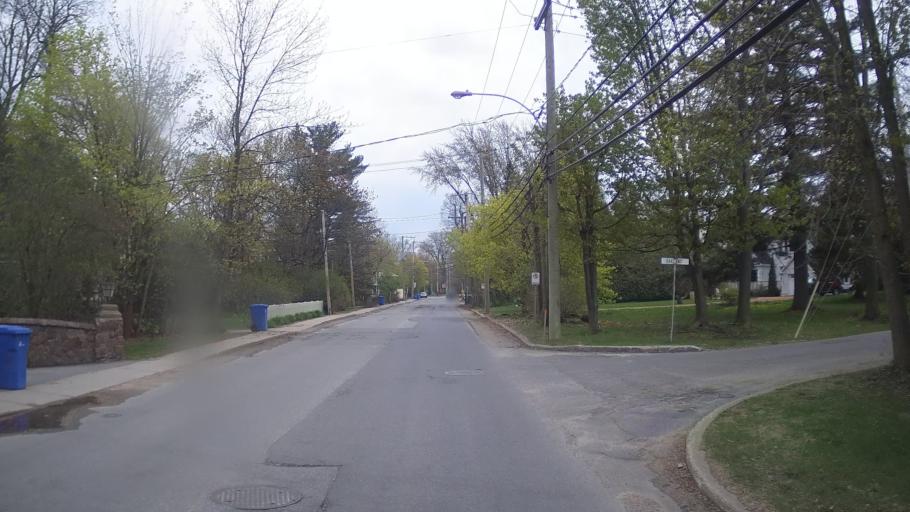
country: CA
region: Quebec
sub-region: Monteregie
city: Hudson
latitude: 45.4626
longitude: -74.1476
